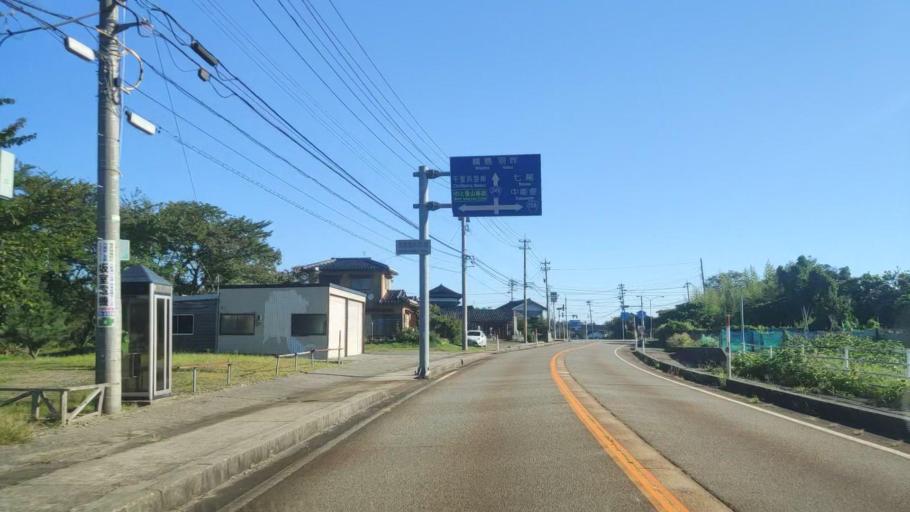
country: JP
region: Ishikawa
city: Hakui
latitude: 36.8429
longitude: 136.7653
